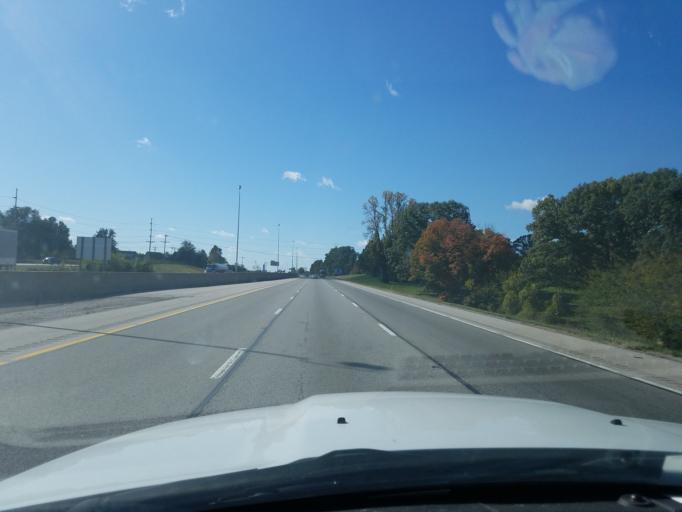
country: US
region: Kentucky
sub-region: Warren County
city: Bowling Green
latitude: 36.9511
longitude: -86.4081
